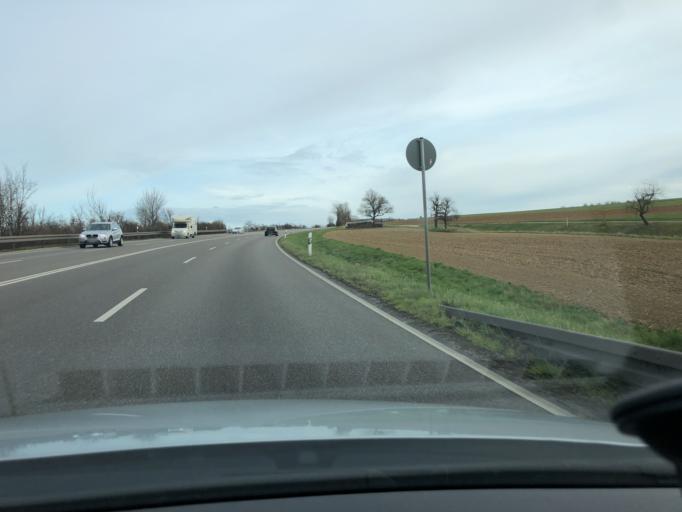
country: DE
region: Baden-Wuerttemberg
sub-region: Regierungsbezirk Stuttgart
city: Oberriexingen
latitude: 48.9185
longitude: 9.0017
